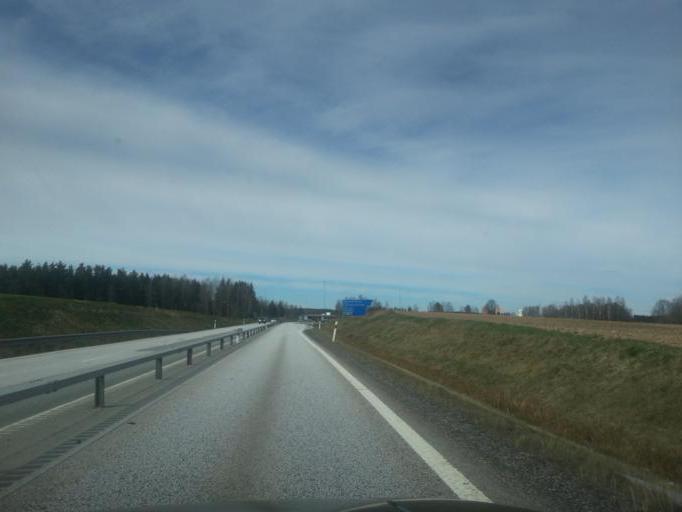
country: SE
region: Joenkoeping
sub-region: Jonkopings Kommun
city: Bankeryd
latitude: 57.8243
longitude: 14.1025
